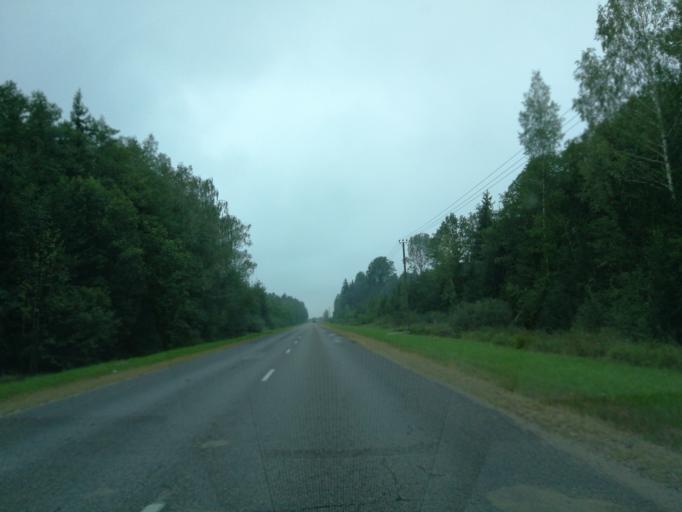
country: LV
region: Varkava
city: Vecvarkava
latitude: 56.3224
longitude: 26.4141
